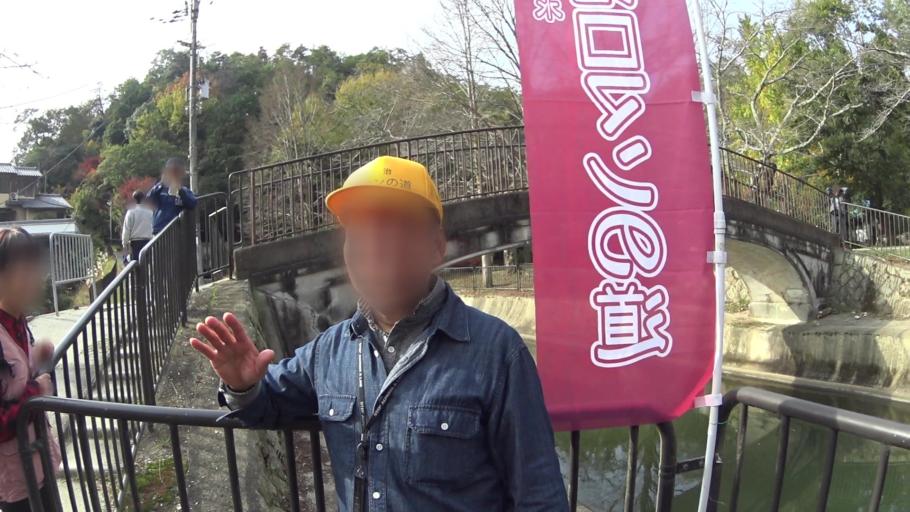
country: JP
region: Kyoto
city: Kyoto
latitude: 35.0005
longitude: 135.8028
